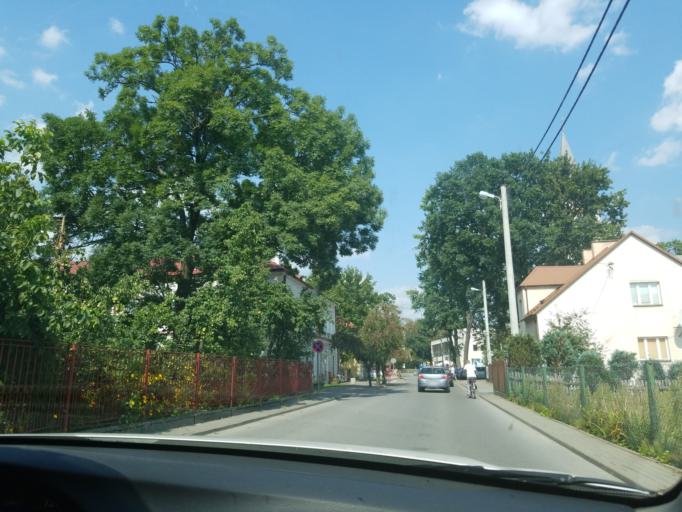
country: PL
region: Subcarpathian Voivodeship
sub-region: Powiat nizanski
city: Nisko
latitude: 50.5178
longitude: 22.1410
